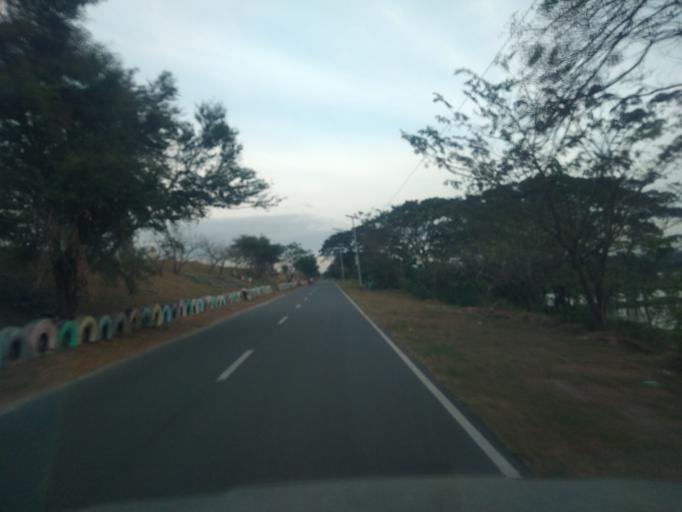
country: PH
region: Central Luzon
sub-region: Province of Pampanga
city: Santa Rita
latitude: 15.0182
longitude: 120.6071
